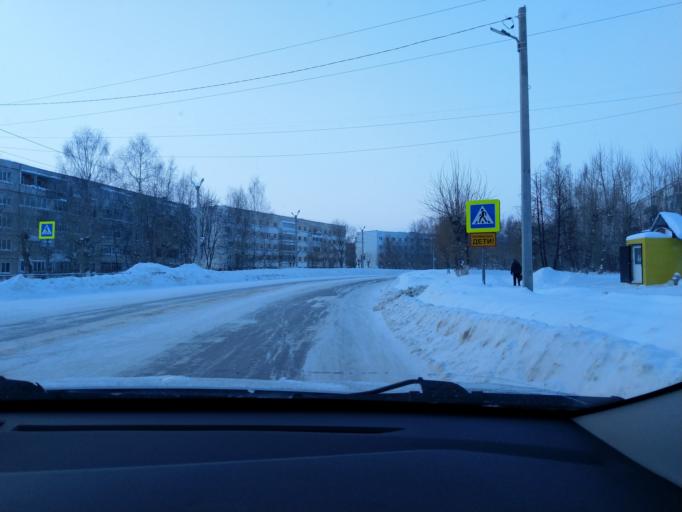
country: RU
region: Perm
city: Dobryanka
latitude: 58.4637
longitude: 56.3969
